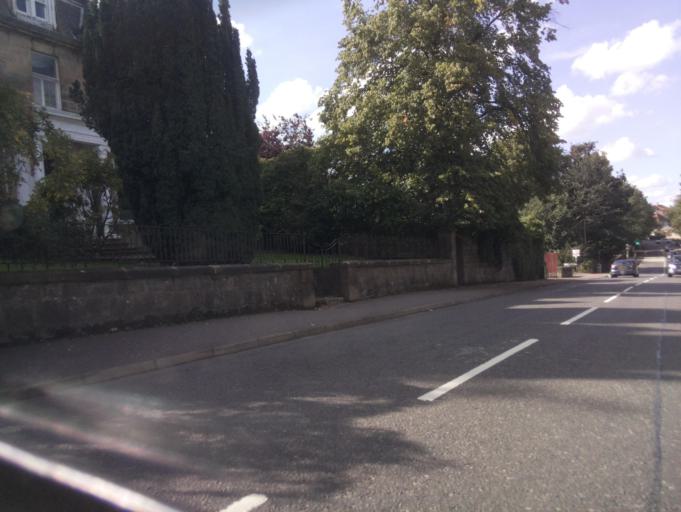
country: GB
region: Scotland
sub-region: Stirling
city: Bannockburn
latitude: 56.0916
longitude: -3.9142
